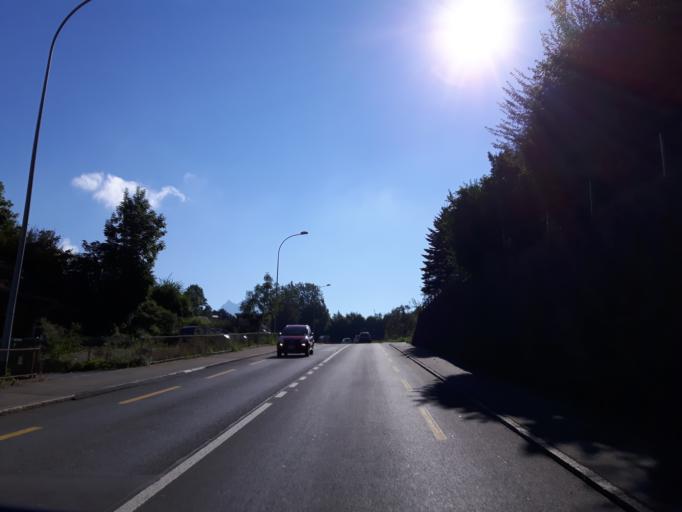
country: CH
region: Schwyz
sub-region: Bezirk Schwyz
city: Goldau
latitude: 47.0526
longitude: 8.5380
